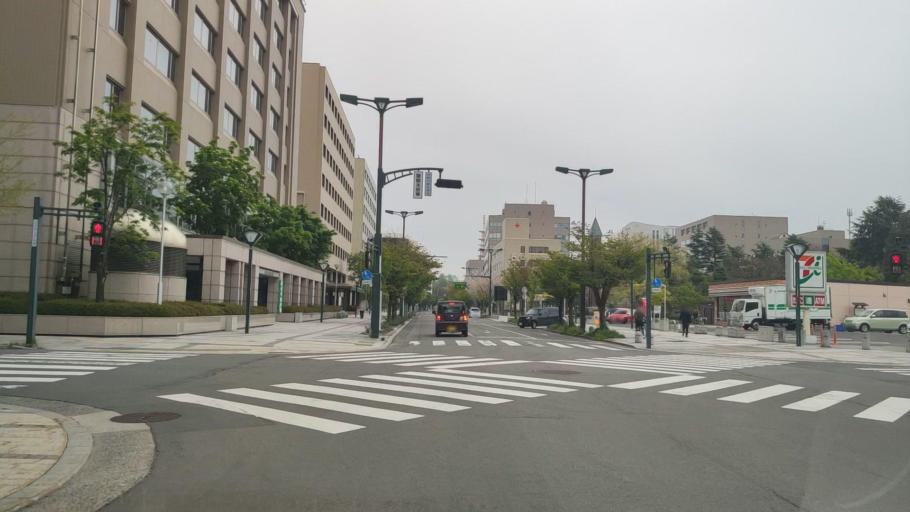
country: JP
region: Aomori
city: Aomori Shi
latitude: 40.8251
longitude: 140.7410
